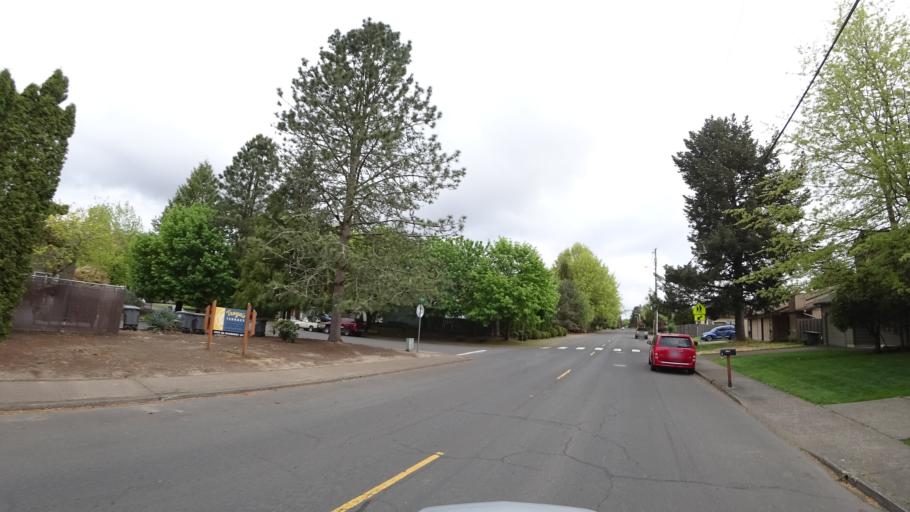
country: US
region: Oregon
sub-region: Washington County
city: Hillsboro
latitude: 45.5326
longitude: -122.9607
